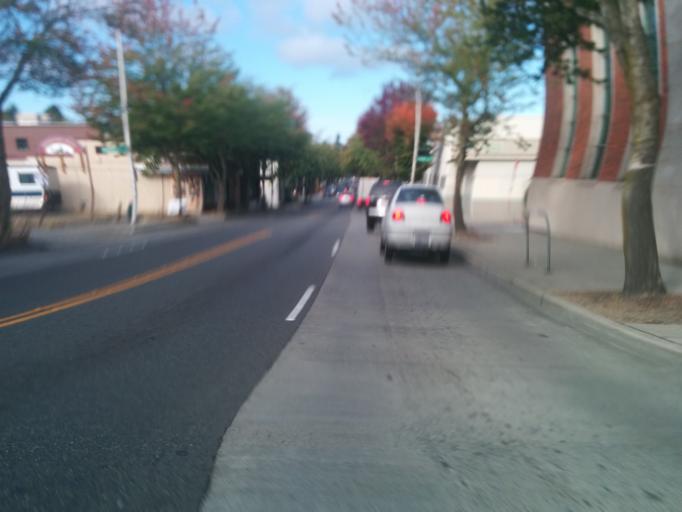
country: US
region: Washington
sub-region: King County
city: Shoreline
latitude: 47.6906
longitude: -122.3535
